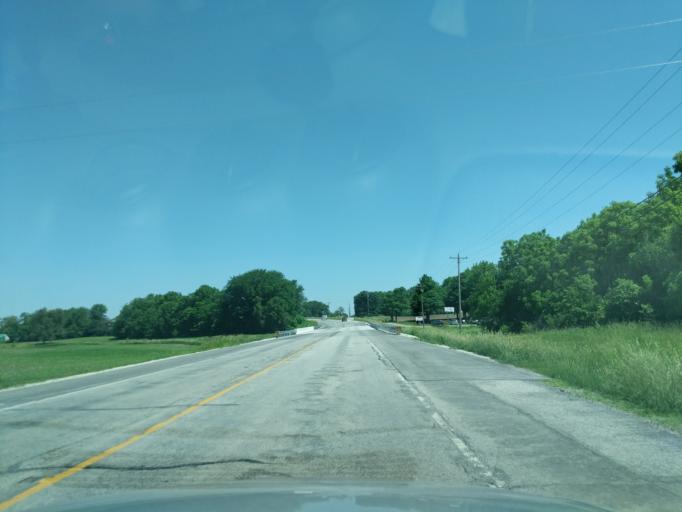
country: US
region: Indiana
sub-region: Whitley County
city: Columbia City
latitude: 41.1138
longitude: -85.4715
